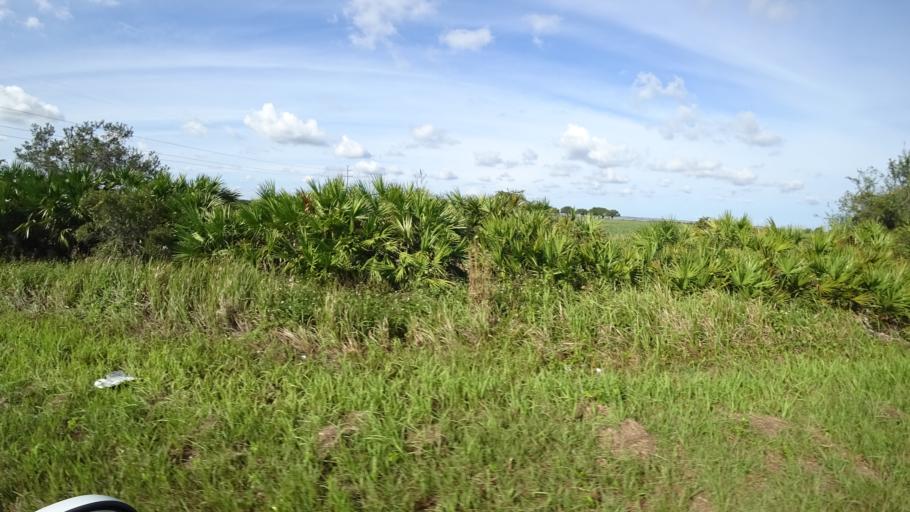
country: US
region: Florida
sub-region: Hillsborough County
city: Wimauma
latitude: 27.6039
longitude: -82.2928
